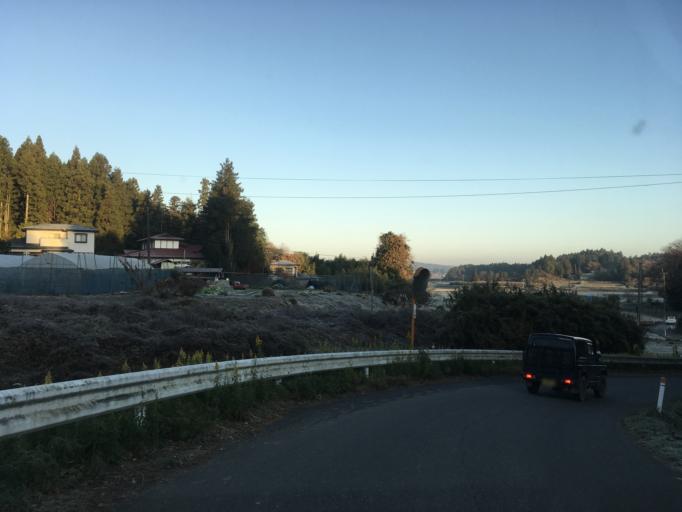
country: JP
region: Iwate
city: Ichinoseki
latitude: 38.7918
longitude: 141.1851
